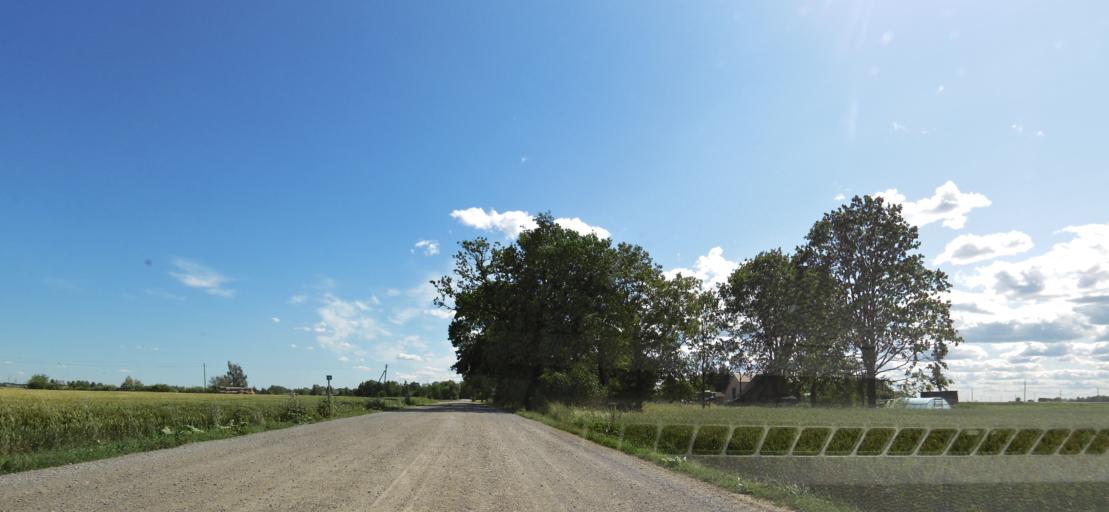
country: LT
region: Panevezys
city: Pasvalys
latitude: 56.1784
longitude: 24.2104
